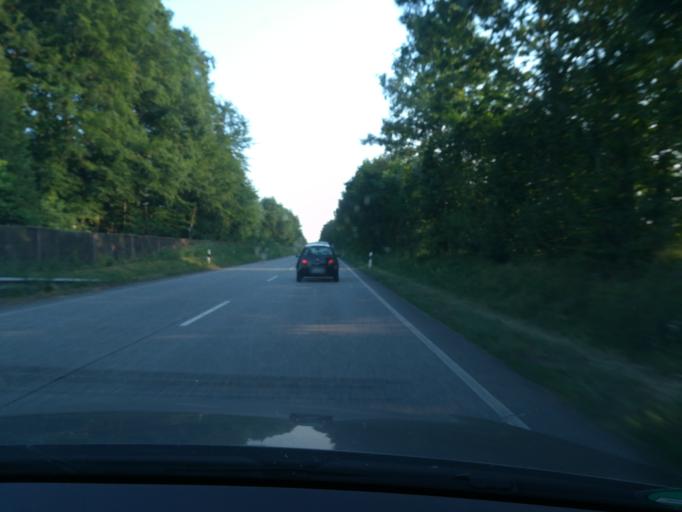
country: DE
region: Schleswig-Holstein
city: Kasseburg
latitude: 53.5499
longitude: 10.4167
